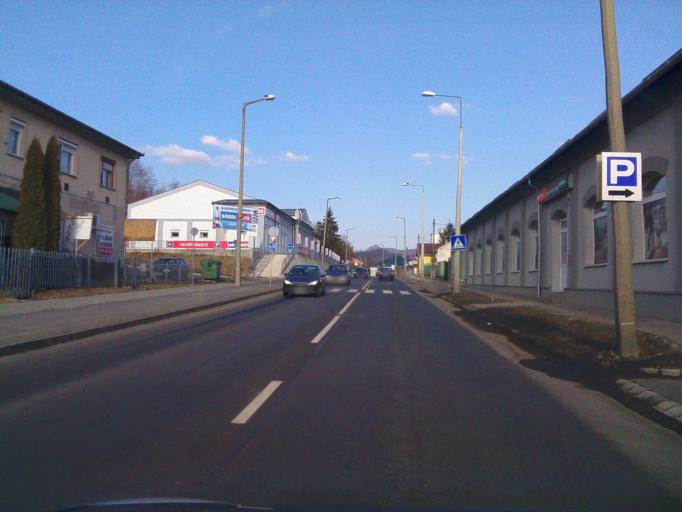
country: HU
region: Nograd
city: Salgotarjan
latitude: 48.0978
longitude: 19.7985
